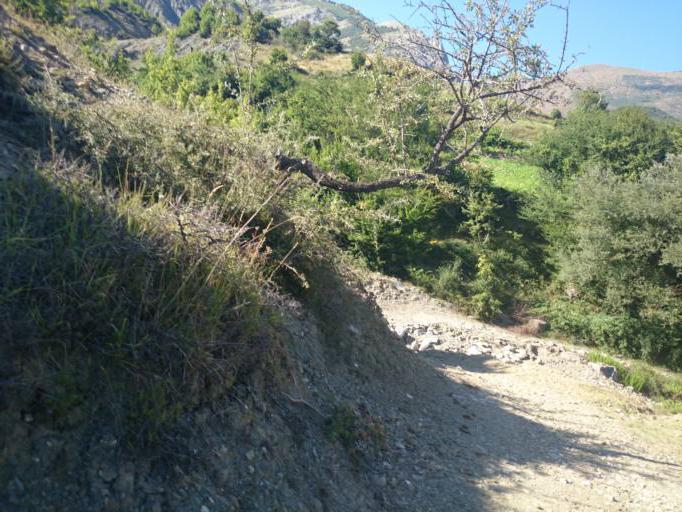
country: AL
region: Elbasan
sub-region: Rrethi i Gramshit
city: Kukur
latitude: 40.8665
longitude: 20.3559
